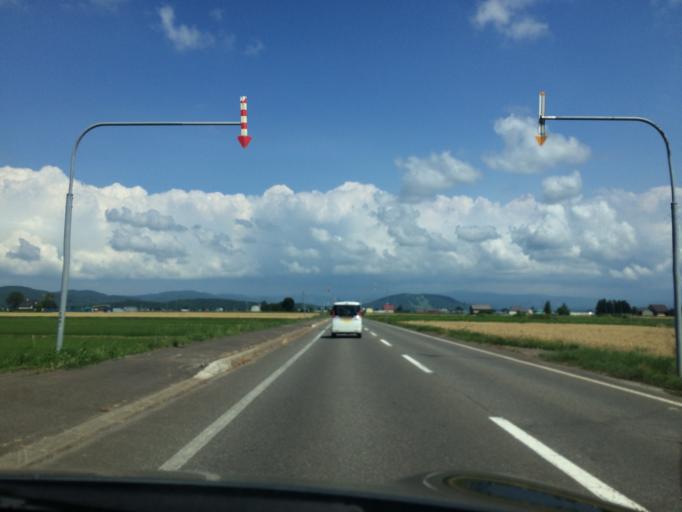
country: JP
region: Hokkaido
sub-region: Asahikawa-shi
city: Asahikawa
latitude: 43.7438
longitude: 142.4474
